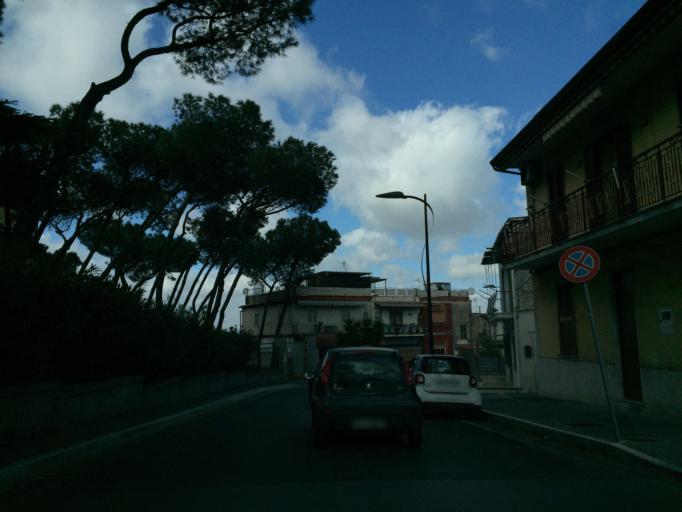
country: IT
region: Campania
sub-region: Provincia di Napoli
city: Massa di Somma
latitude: 40.8468
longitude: 14.3731
